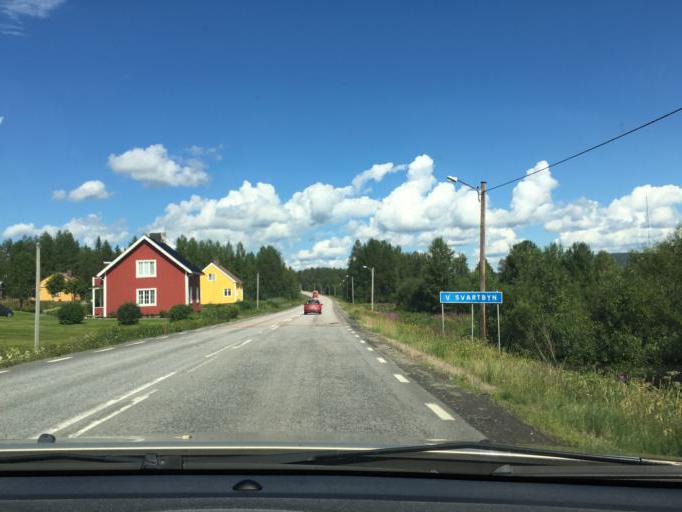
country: SE
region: Norrbotten
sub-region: Overkalix Kommun
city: OEverkalix
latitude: 66.2800
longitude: 22.8184
